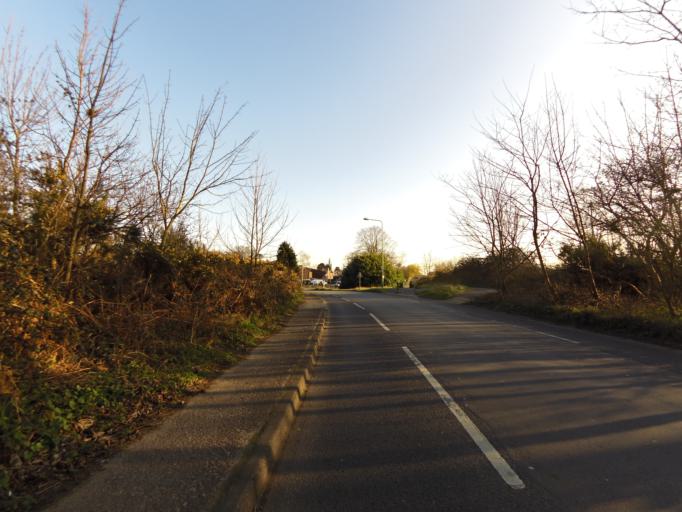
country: GB
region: England
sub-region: Suffolk
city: Kesgrave
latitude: 52.0659
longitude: 1.2796
